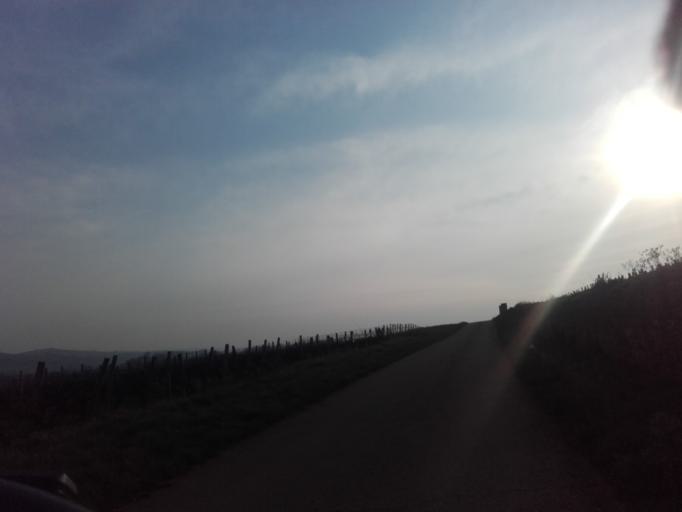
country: FR
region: Bourgogne
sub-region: Departement de la Cote-d'Or
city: Nolay
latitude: 46.9095
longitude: 4.6809
